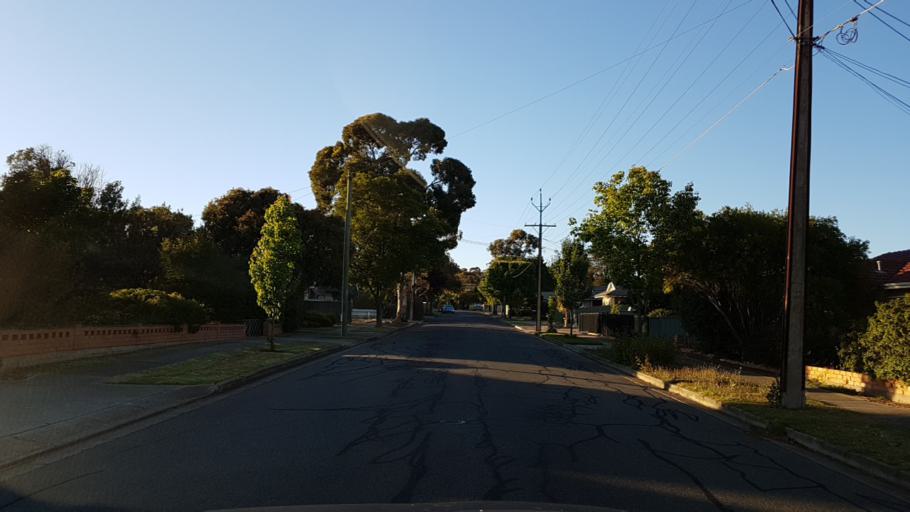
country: AU
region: South Australia
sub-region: Marion
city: Sturt
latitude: -35.0201
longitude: 138.5529
